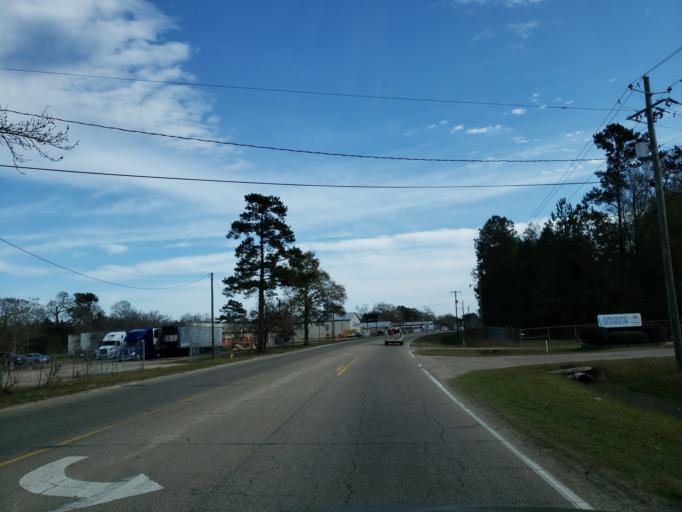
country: US
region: Mississippi
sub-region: Forrest County
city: Glendale
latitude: 31.3462
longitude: -89.3145
